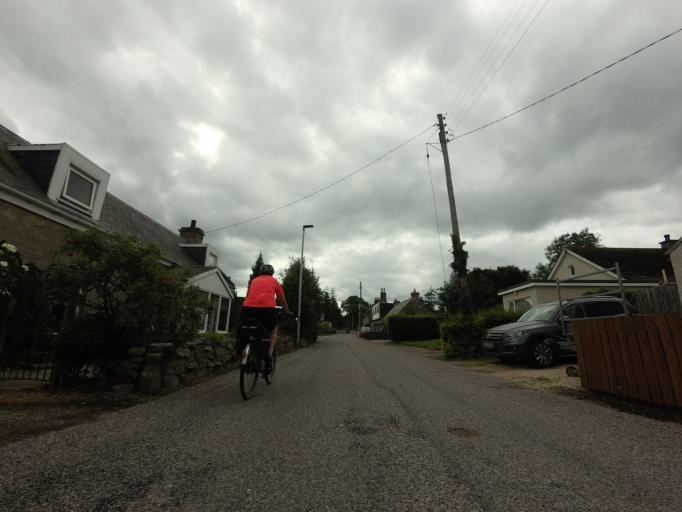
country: GB
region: Scotland
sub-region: Moray
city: Forres
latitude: 57.6062
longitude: -3.6920
